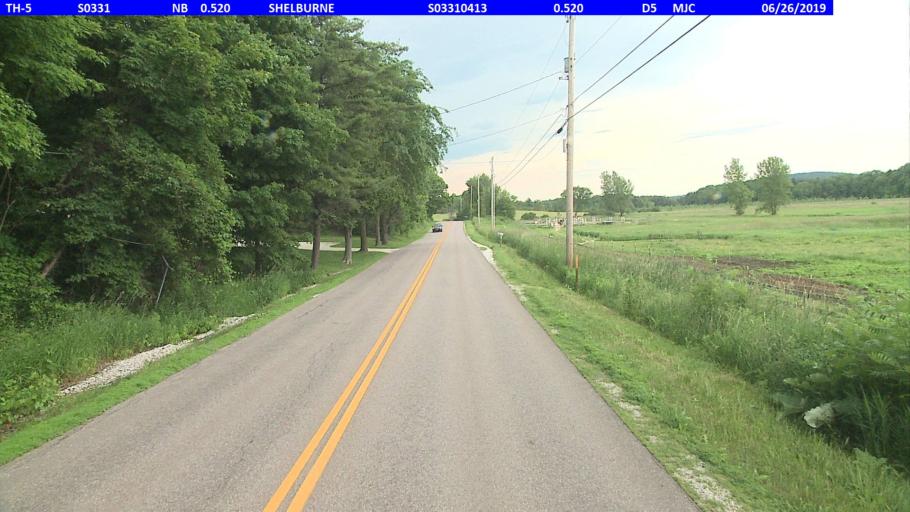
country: US
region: Vermont
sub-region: Chittenden County
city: Hinesburg
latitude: 44.3787
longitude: -73.1784
